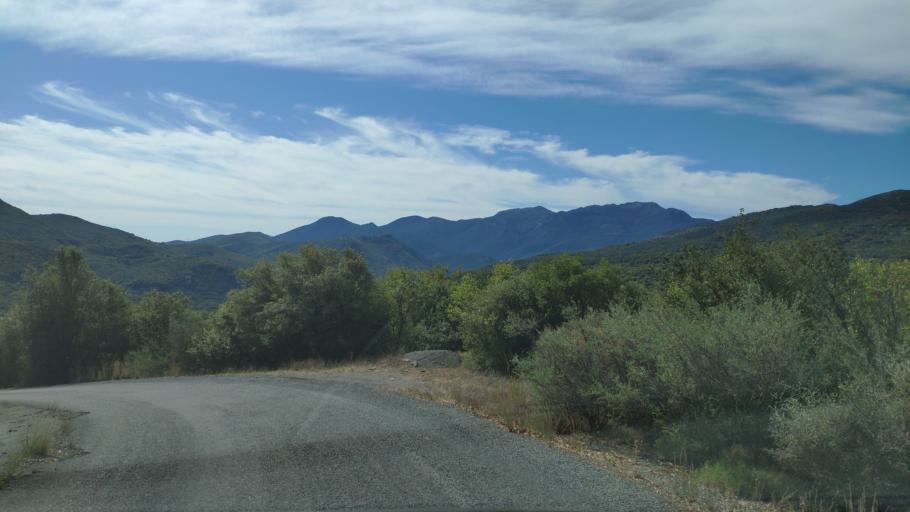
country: GR
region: Peloponnese
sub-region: Nomos Arkadias
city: Dimitsana
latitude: 37.5402
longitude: 22.0497
